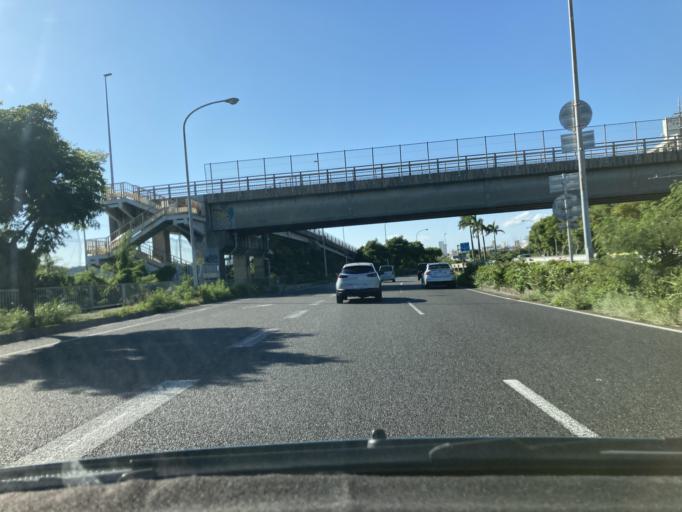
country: JP
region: Okinawa
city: Ginowan
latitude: 26.2493
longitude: 127.7443
